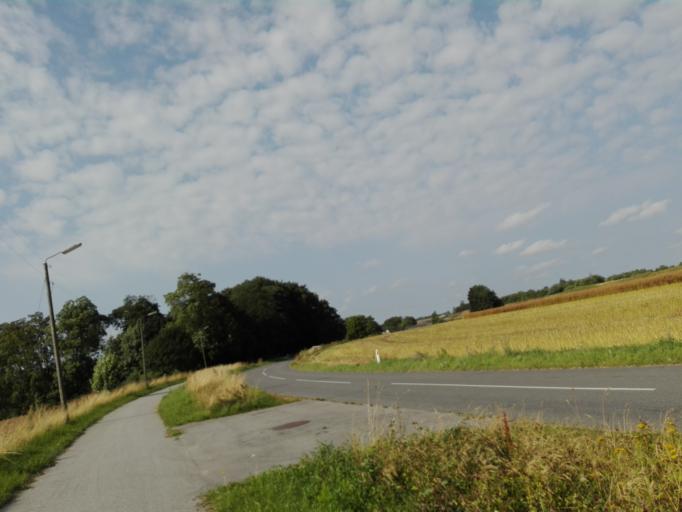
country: DK
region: Central Jutland
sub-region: Arhus Kommune
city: Trige
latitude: 56.2152
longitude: 10.1854
